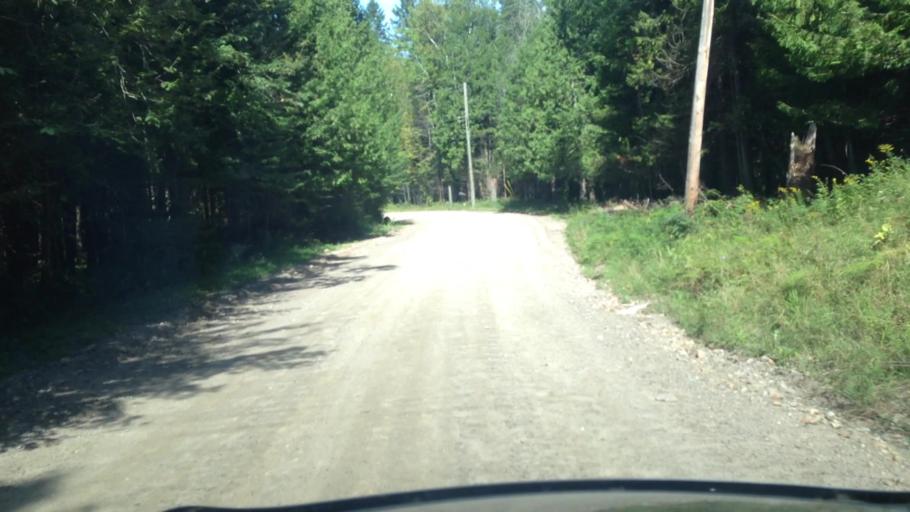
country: CA
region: Quebec
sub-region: Laurentides
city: Mont-Tremblant
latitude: 45.9446
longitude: -74.5896
